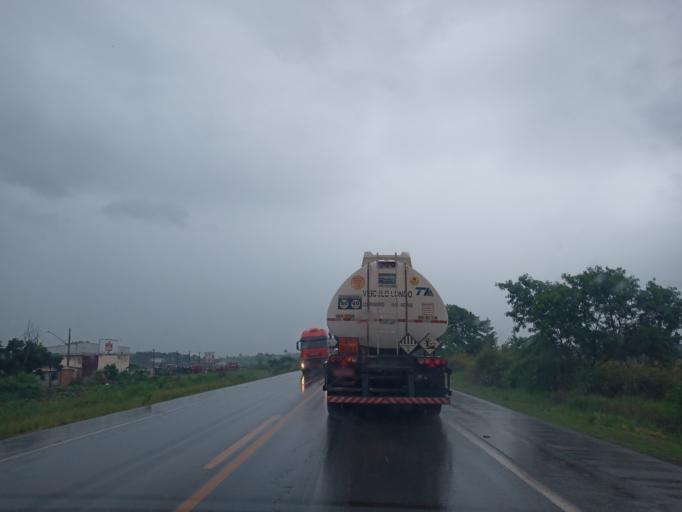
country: BR
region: Minas Gerais
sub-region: Luz
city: Luz
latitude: -19.7833
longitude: -45.6918
